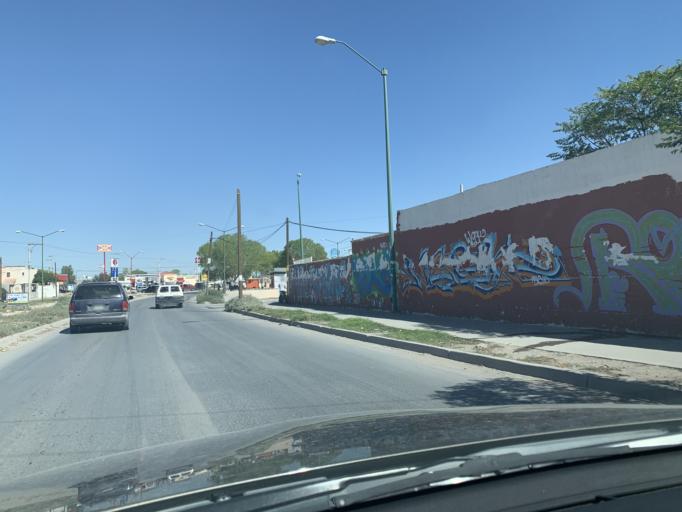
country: US
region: Texas
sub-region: El Paso County
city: Socorro Mission Number 1 Colonia
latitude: 31.6002
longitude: -106.3577
